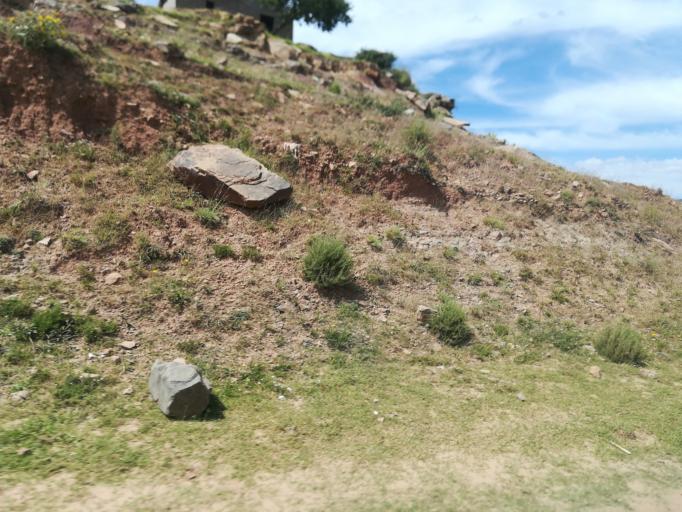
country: LS
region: Mohale's Hoek District
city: Mohale's Hoek
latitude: -30.1142
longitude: 27.4712
